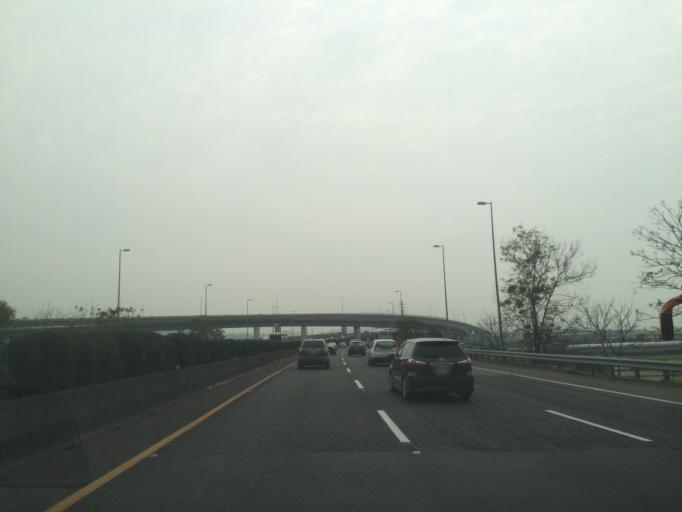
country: TW
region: Taiwan
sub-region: Taichung City
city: Taichung
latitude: 24.0537
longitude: 120.6773
